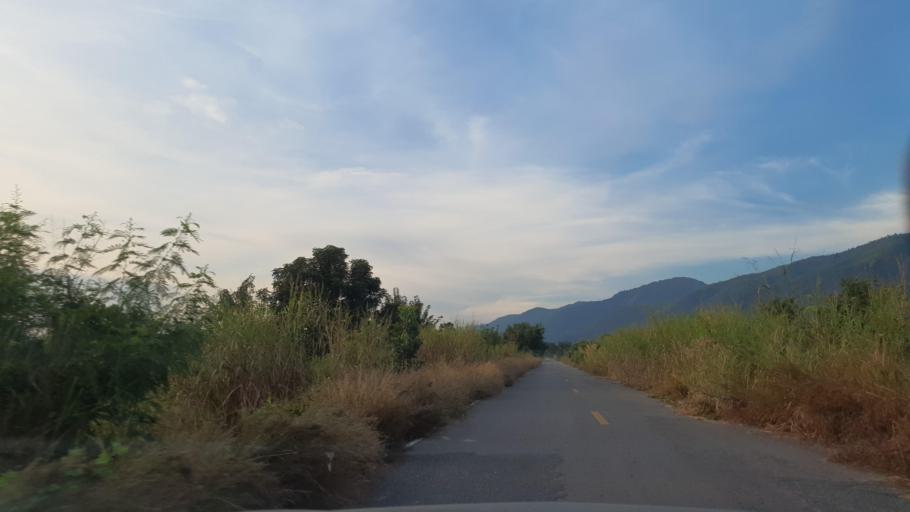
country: TH
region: Uthai Thani
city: Sawang Arom
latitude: 15.7026
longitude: 99.9611
